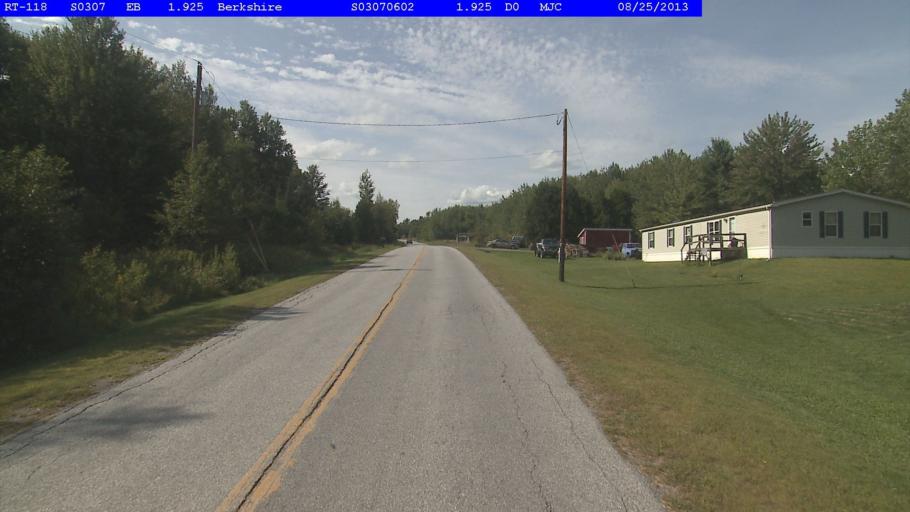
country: US
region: Vermont
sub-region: Franklin County
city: Enosburg Falls
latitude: 44.9469
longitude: -72.7430
